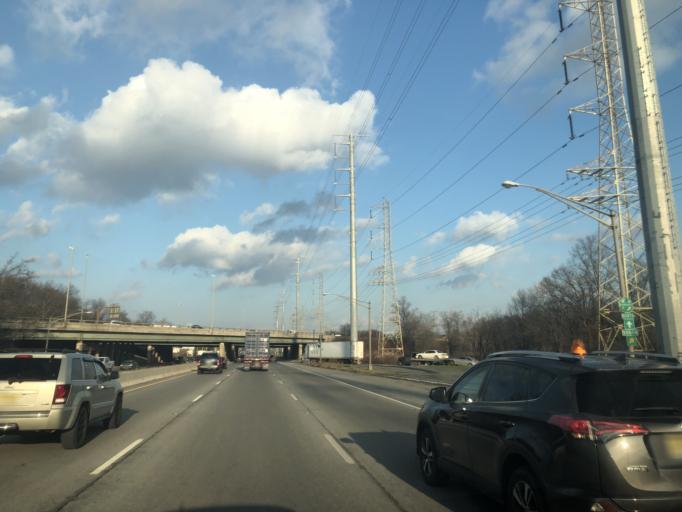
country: US
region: New Jersey
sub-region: Middlesex County
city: Metuchen
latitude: 40.5270
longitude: -74.3560
